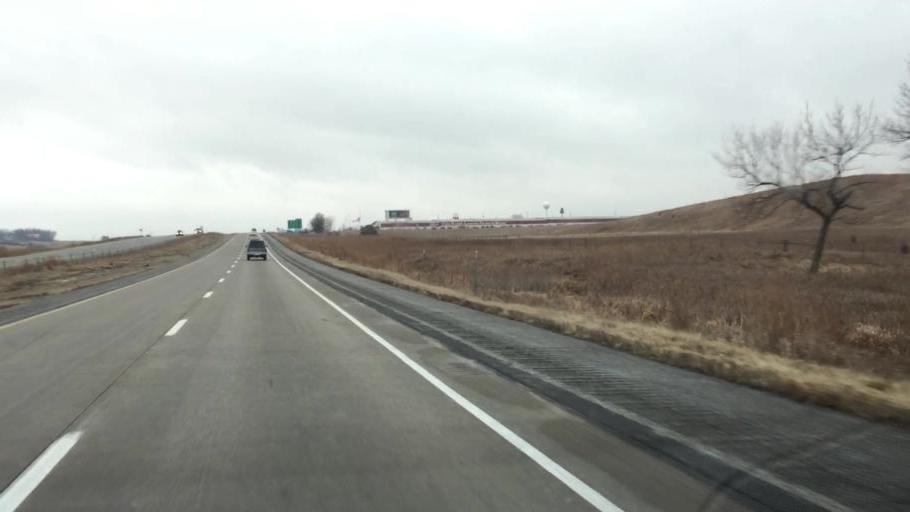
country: US
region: Iowa
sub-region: Iowa County
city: Williamsburg
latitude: 41.6872
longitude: -91.9958
